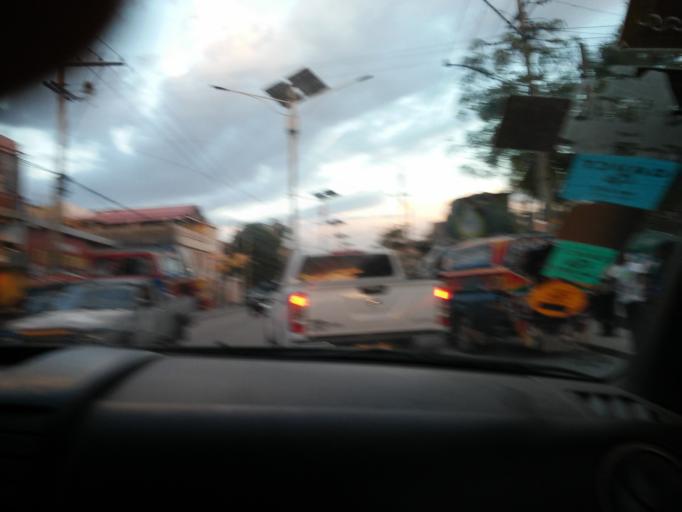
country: HT
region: Ouest
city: Port-au-Prince
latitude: 18.5565
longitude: -72.3245
